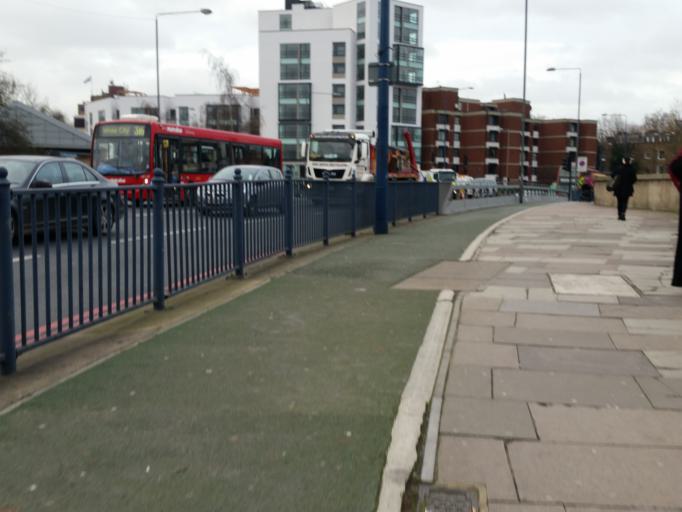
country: GB
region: England
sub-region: Greater London
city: Hammersmith
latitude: 51.5042
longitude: -0.2173
